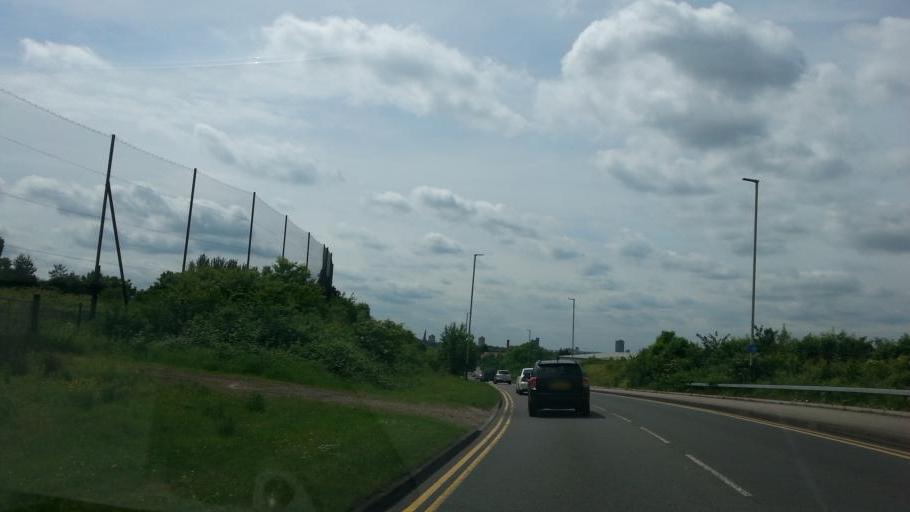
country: GB
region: England
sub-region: Leicestershire
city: Syston
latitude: 52.6557
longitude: -1.0874
